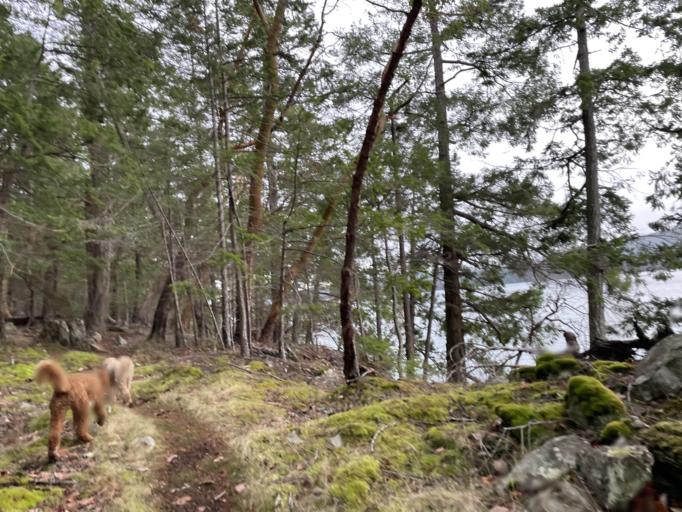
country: CA
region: British Columbia
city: North Cowichan
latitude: 48.9385
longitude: -123.5490
